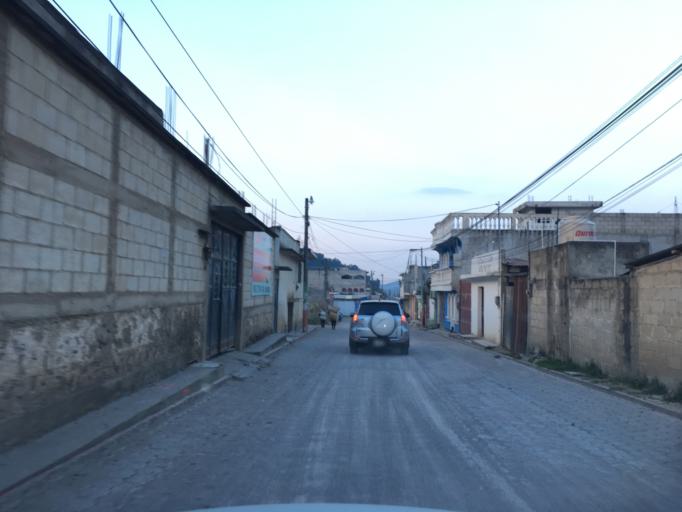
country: GT
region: Chimaltenango
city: Tecpan Guatemala
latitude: 14.7581
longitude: -91.0006
